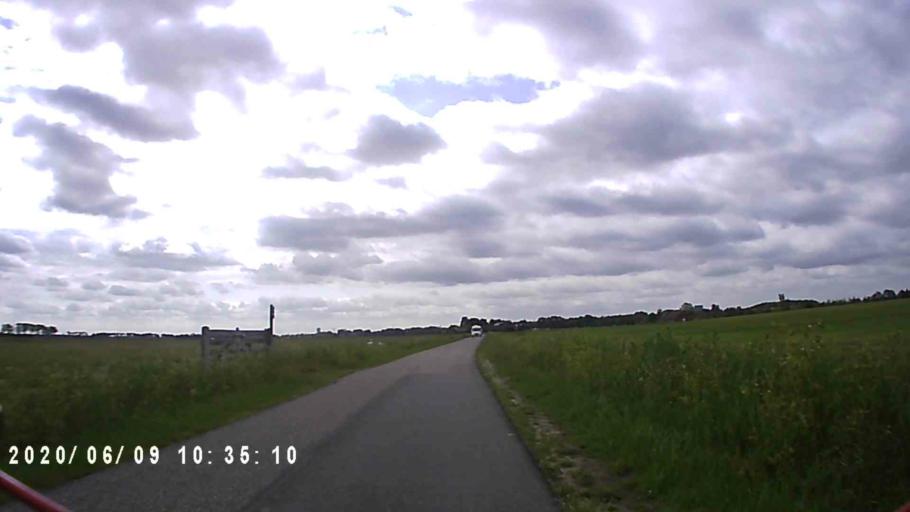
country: NL
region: Groningen
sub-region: Gemeente Groningen
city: Korrewegwijk
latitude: 53.2612
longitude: 6.5226
